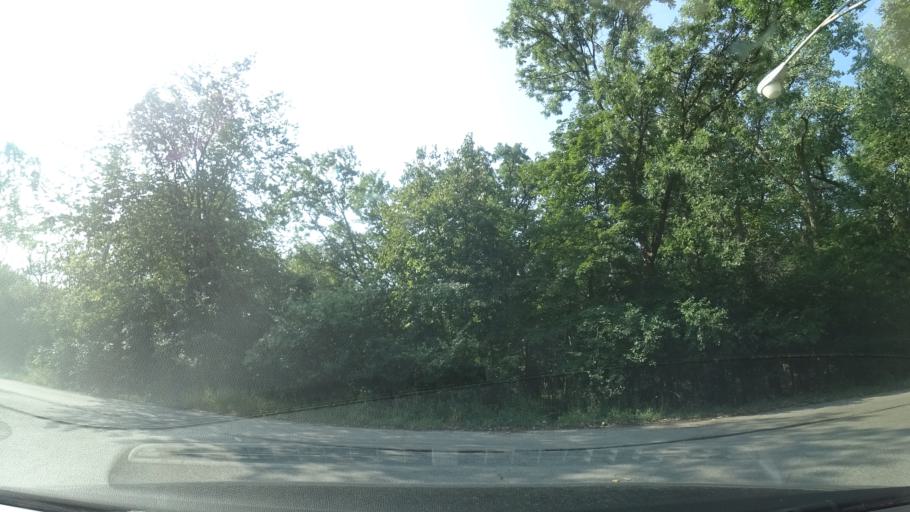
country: US
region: Illinois
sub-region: Cook County
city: Lincolnwood
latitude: 41.9827
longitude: -87.7408
